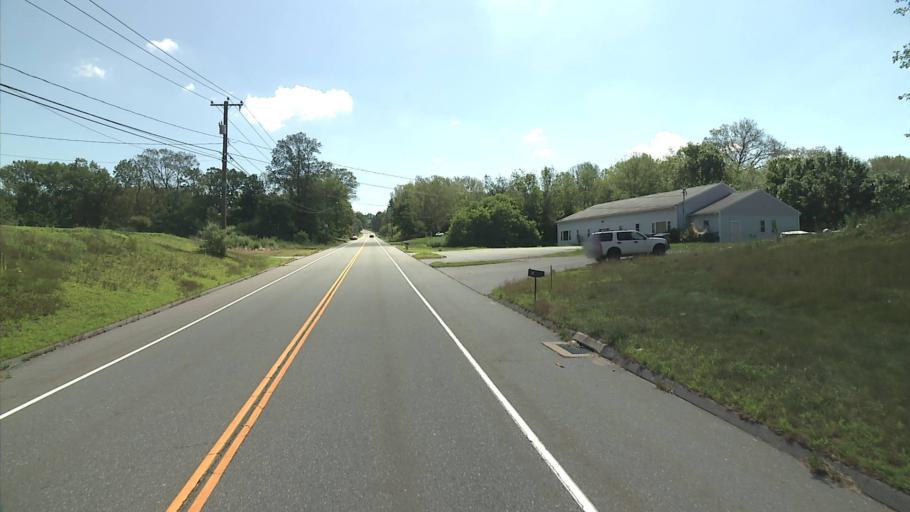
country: US
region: Connecticut
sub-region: Windham County
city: Plainfield
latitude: 41.6818
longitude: -71.8991
